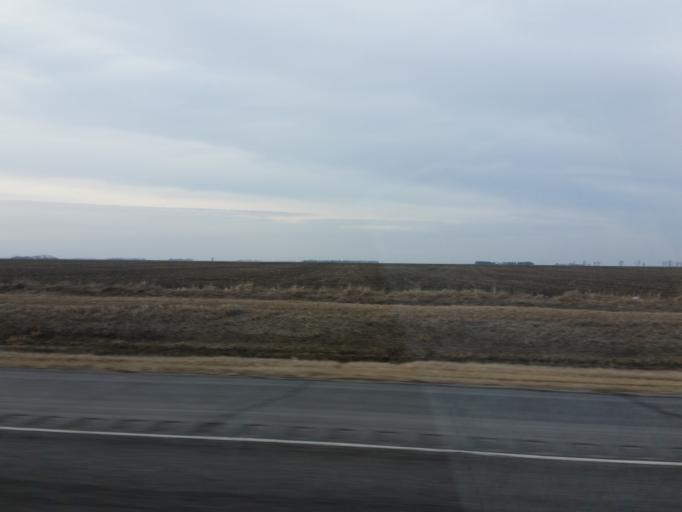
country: US
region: North Dakota
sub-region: Cass County
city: Casselton
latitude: 46.8768
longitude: -97.1258
